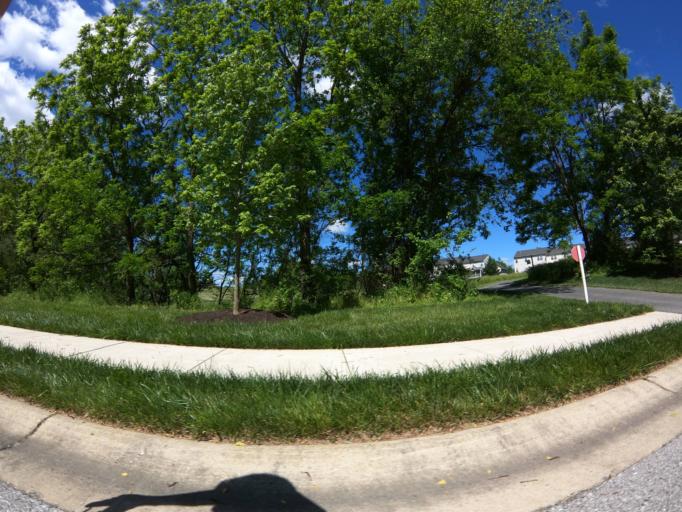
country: US
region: Maryland
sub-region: Howard County
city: Columbia
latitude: 39.3136
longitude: -76.8902
